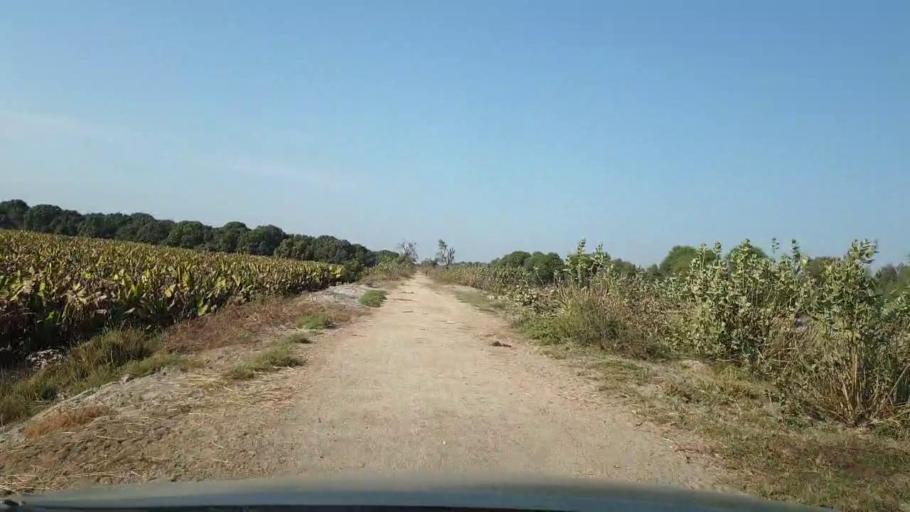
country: PK
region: Sindh
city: Tando Adam
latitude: 25.6033
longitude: 68.6249
